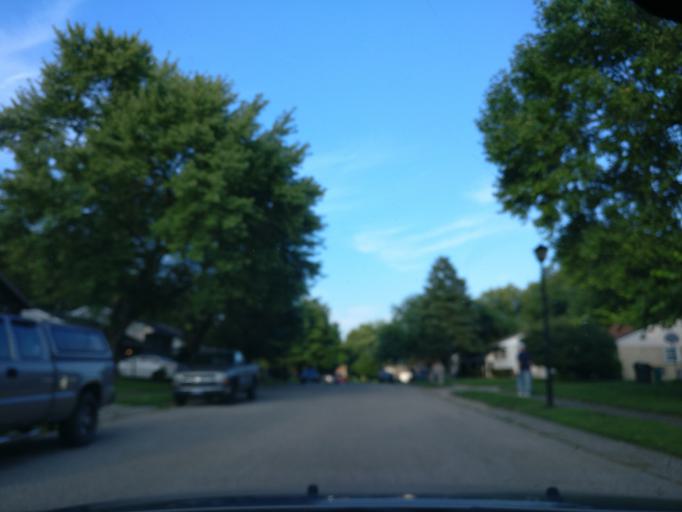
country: US
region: Ohio
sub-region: Warren County
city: Springboro
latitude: 39.5723
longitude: -84.2487
